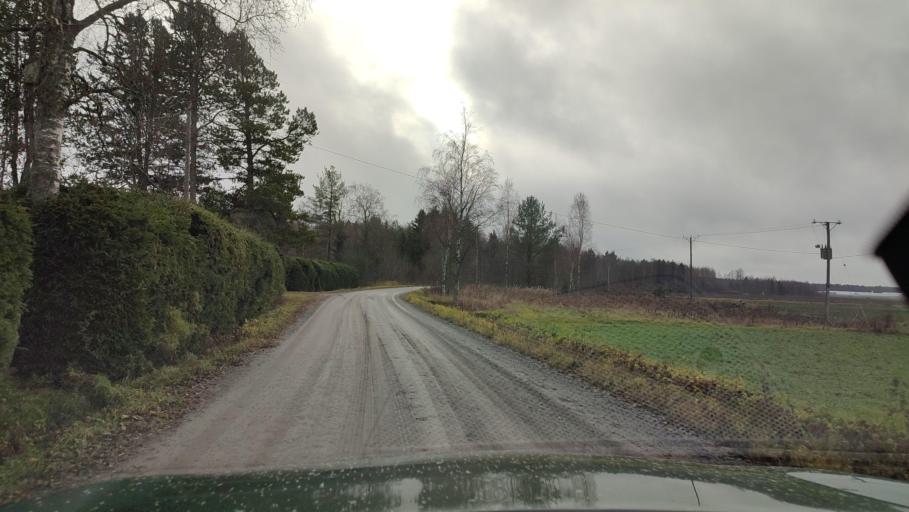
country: FI
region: Ostrobothnia
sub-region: Sydosterbotten
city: Naerpes
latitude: 62.4512
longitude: 21.4567
